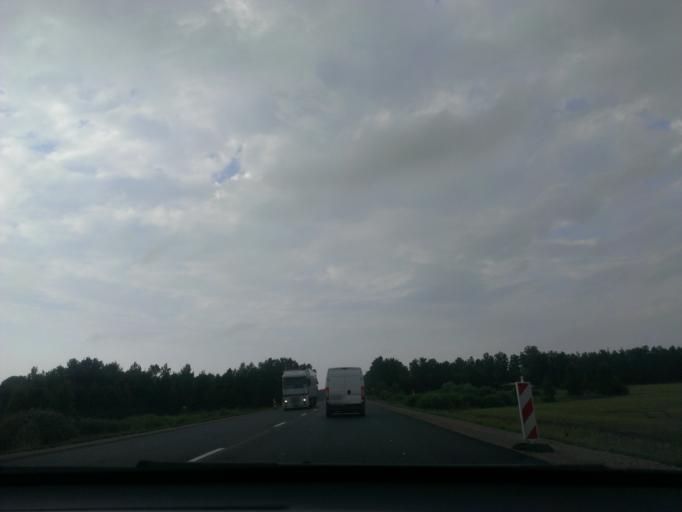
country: LV
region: Lecava
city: Iecava
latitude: 56.6388
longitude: 24.2261
